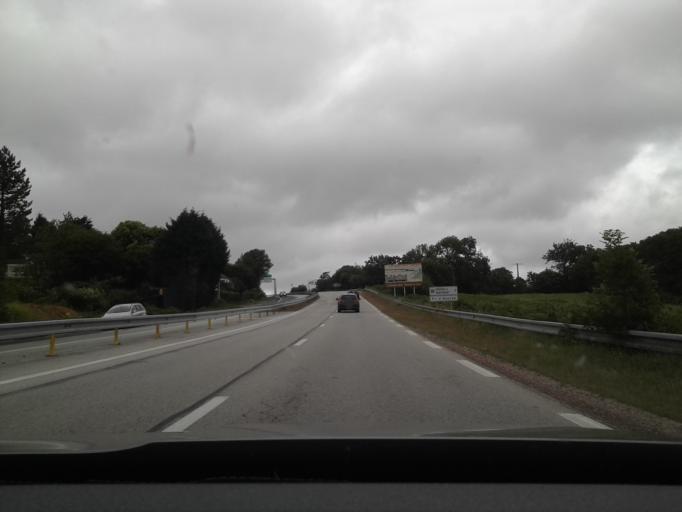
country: FR
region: Lower Normandy
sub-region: Departement de la Manche
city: La Glacerie
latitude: 49.5919
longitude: -1.5959
